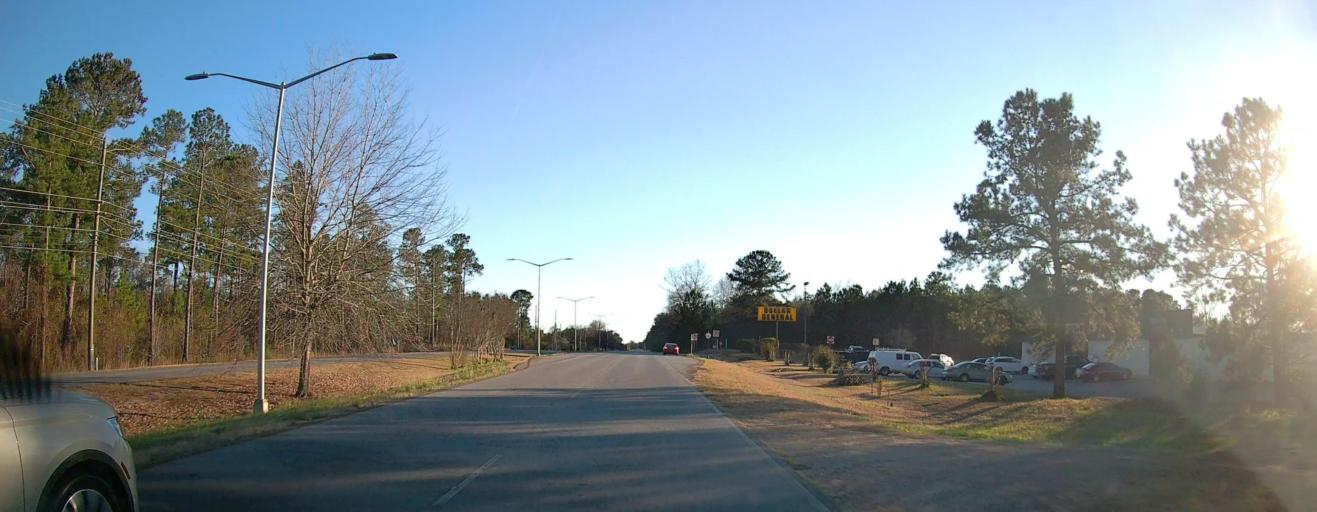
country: US
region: Georgia
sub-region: Dougherty County
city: Albany
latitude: 31.5741
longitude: -84.2207
